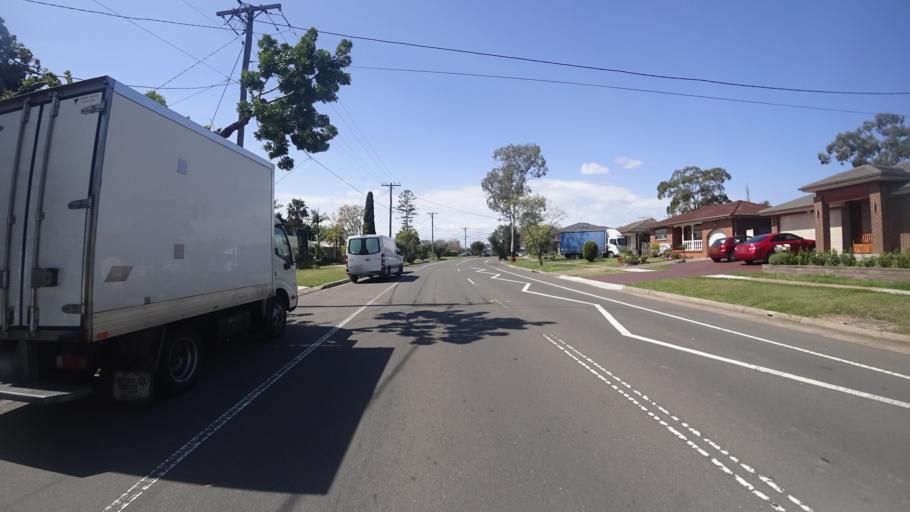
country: AU
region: New South Wales
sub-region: Liverpool
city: Miller
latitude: -33.9335
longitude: 150.8932
